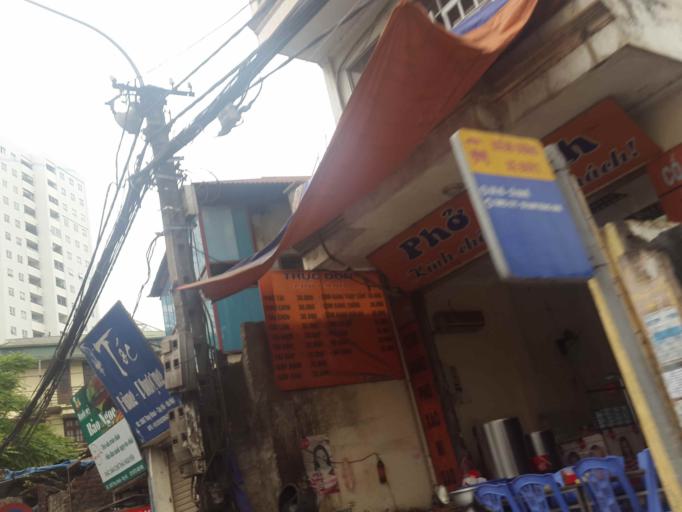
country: VN
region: Ha Noi
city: Cau Giay
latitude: 21.0433
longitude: 105.8177
